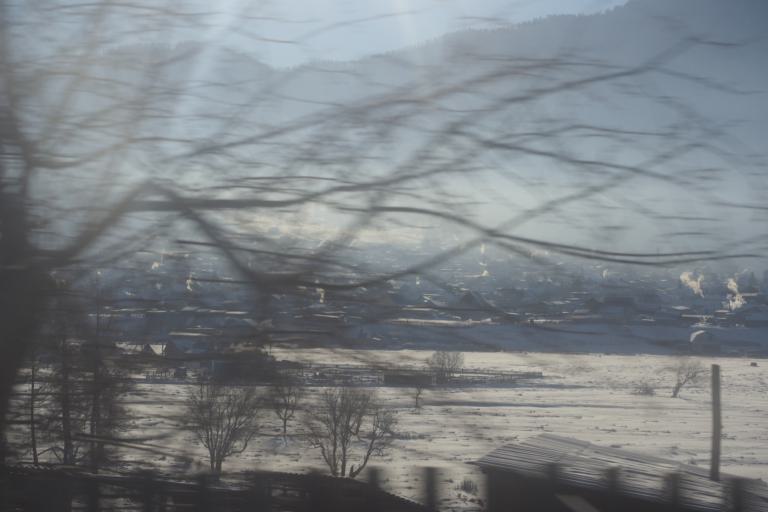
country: RU
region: Altay
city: Onguday
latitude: 50.7596
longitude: 86.1270
